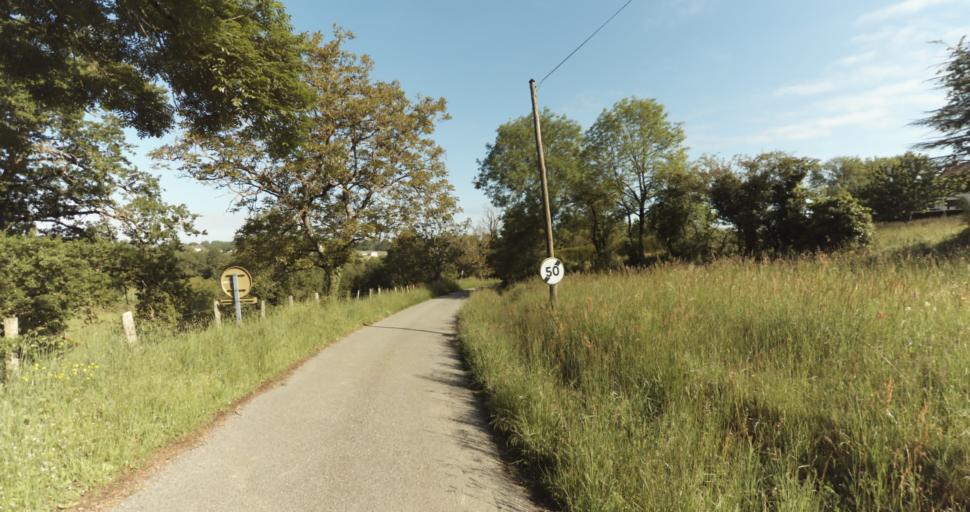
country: FR
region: Limousin
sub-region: Departement de la Haute-Vienne
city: Solignac
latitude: 45.7310
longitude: 1.2426
